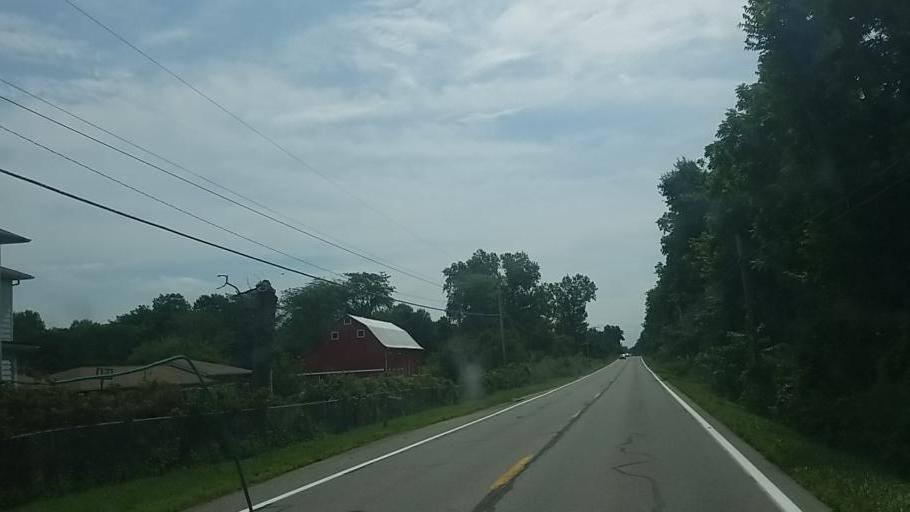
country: US
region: Ohio
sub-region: Delaware County
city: Sunbury
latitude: 40.2282
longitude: -82.8251
